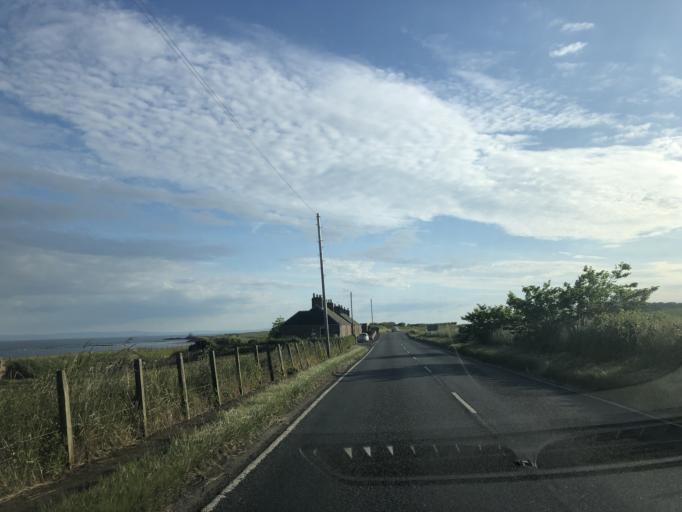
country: GB
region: Scotland
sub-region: Fife
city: Saint Monance
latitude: 56.1960
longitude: -2.7969
